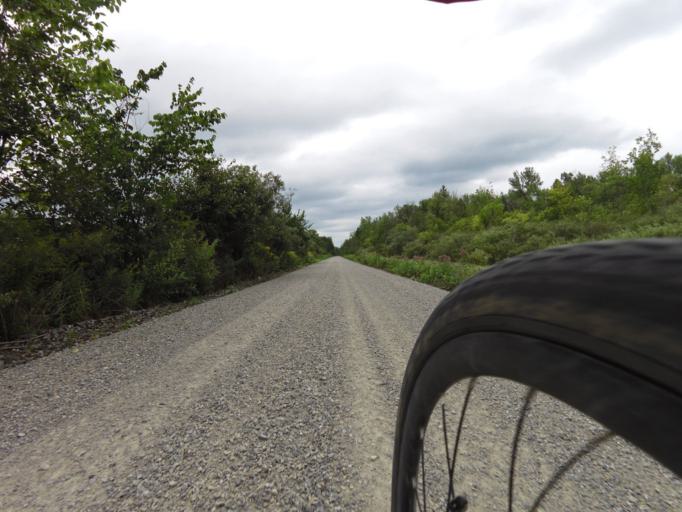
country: CA
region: Ontario
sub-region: Lanark County
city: Smiths Falls
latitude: 44.9564
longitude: -76.0477
